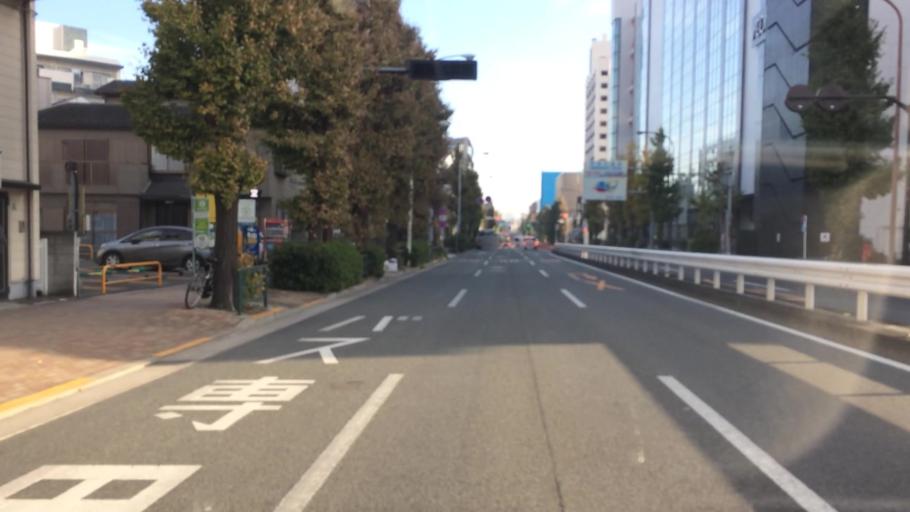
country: JP
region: Tokyo
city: Tokyo
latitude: 35.6222
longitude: 139.6831
